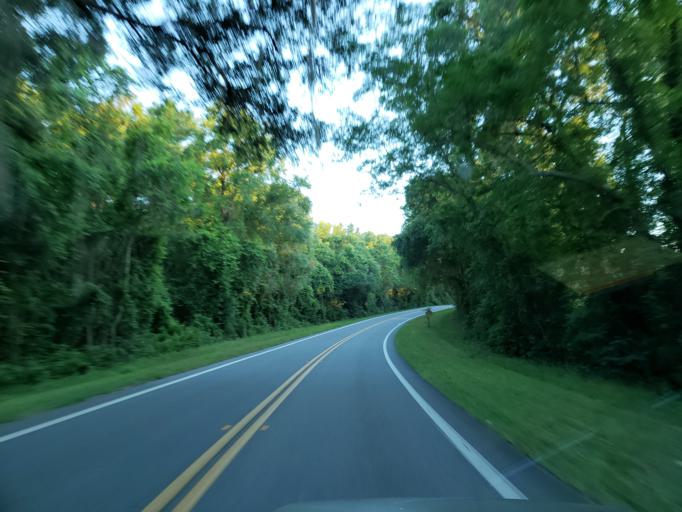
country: US
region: Florida
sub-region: Madison County
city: Madison
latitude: 30.6005
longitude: -83.2541
